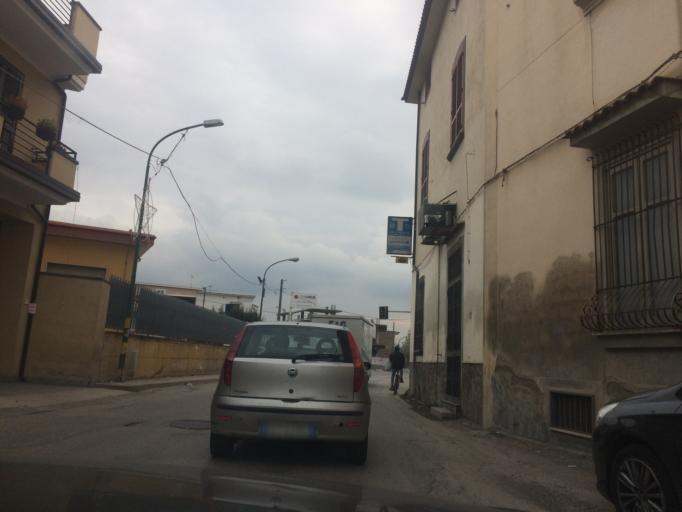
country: IT
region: Campania
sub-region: Provincia di Napoli
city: Piazzolla
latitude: 40.8791
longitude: 14.5285
